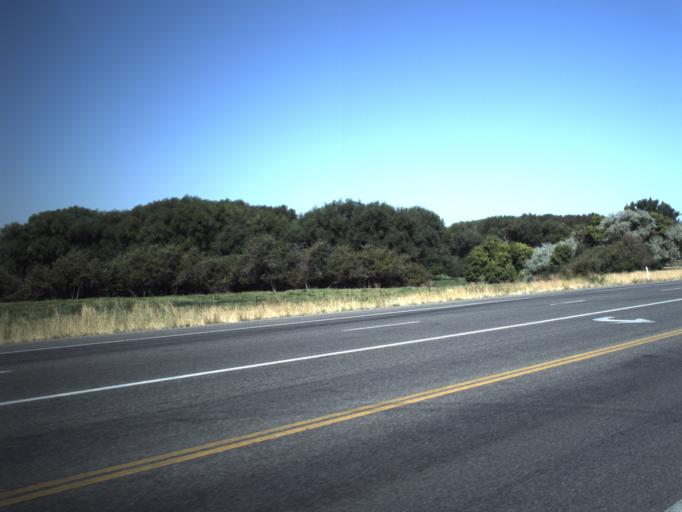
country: US
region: Utah
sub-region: Cache County
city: Millville
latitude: 41.6899
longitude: -111.8341
